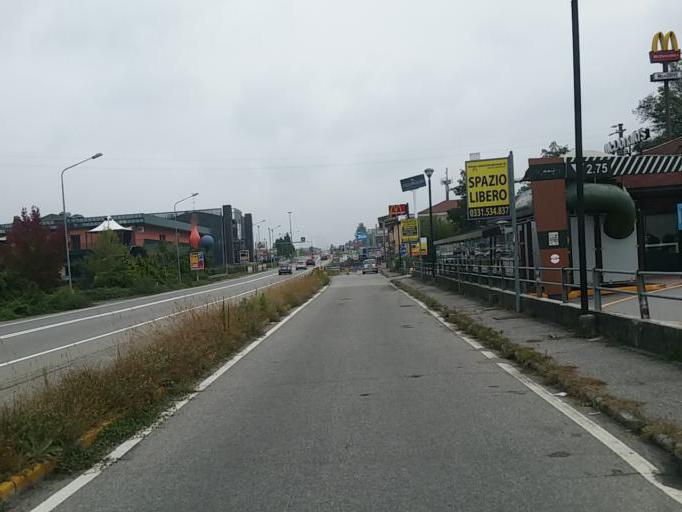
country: IT
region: Lombardy
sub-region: Provincia di Varese
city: Lisanza
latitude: 45.7192
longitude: 8.5992
